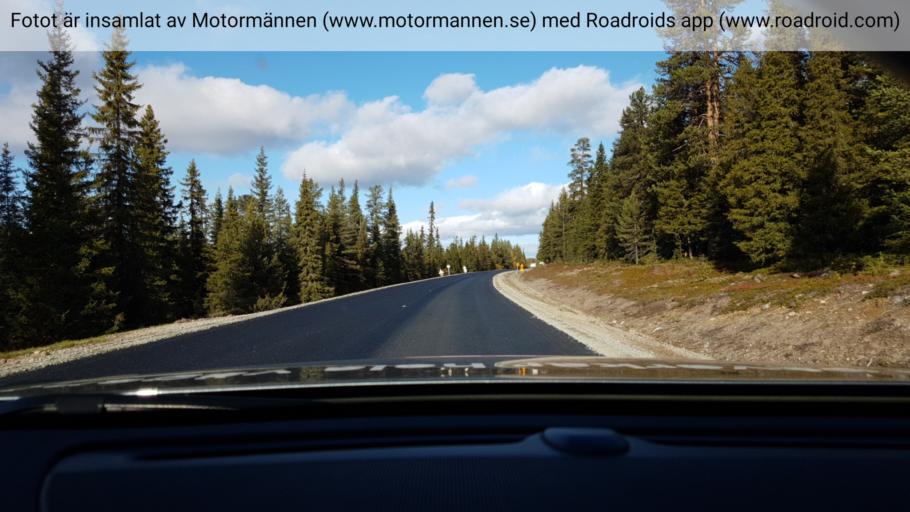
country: SE
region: Norrbotten
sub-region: Arjeplogs Kommun
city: Arjeplog
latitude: 65.9203
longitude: 18.3172
